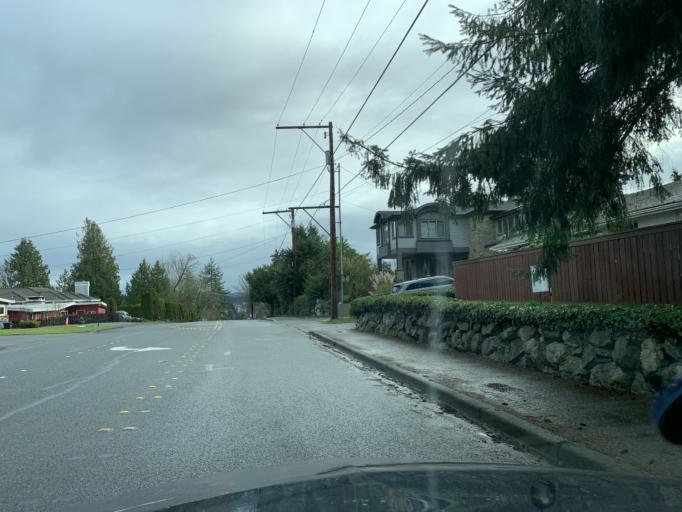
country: US
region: Washington
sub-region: King County
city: Mercer Island
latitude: 47.5891
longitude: -122.2430
